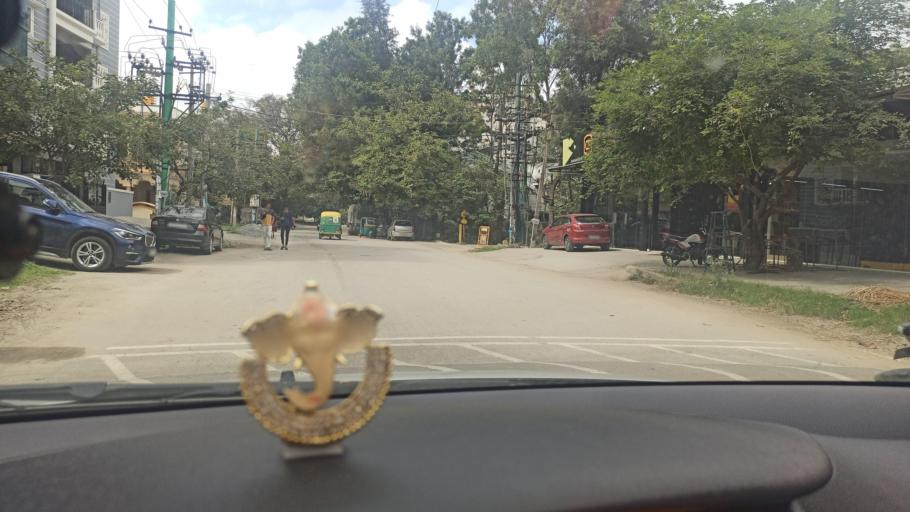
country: IN
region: Karnataka
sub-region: Bangalore Urban
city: Bangalore
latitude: 12.9141
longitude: 77.6285
